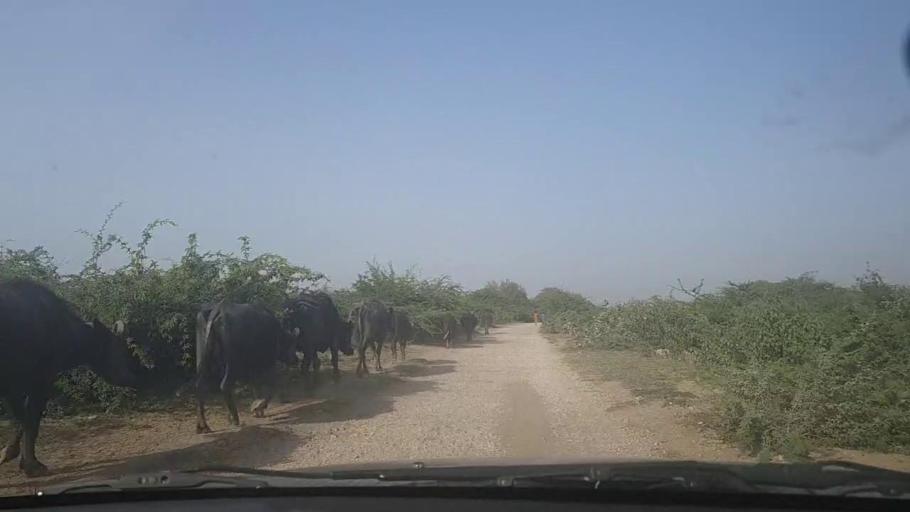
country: PK
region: Sindh
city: Keti Bandar
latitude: 24.2644
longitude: 67.5662
